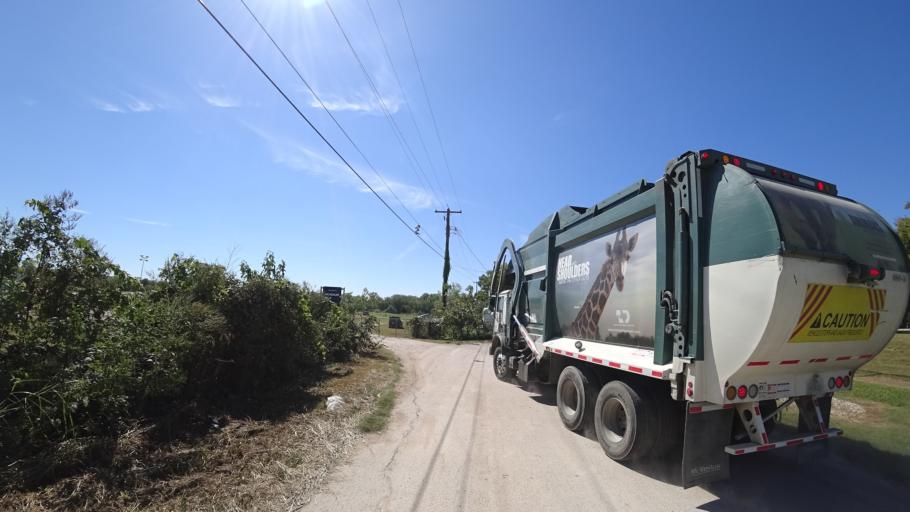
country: US
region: Texas
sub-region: Travis County
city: Hornsby Bend
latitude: 30.2700
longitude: -97.6517
